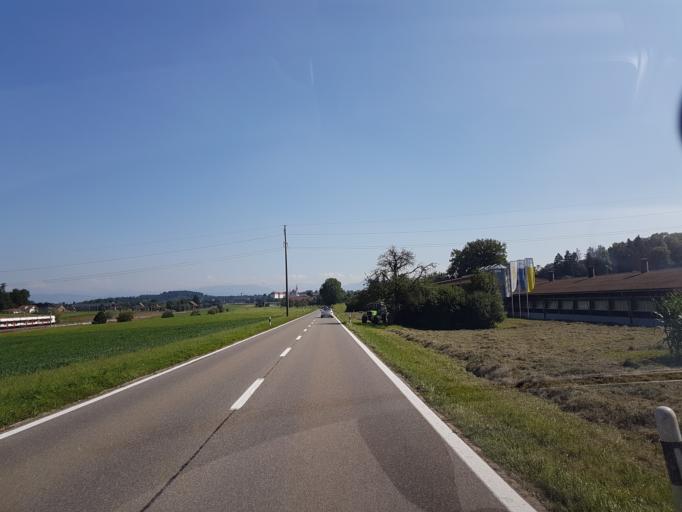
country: CH
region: Aargau
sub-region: Bezirk Muri
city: Muri
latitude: 47.2906
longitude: 8.3231
